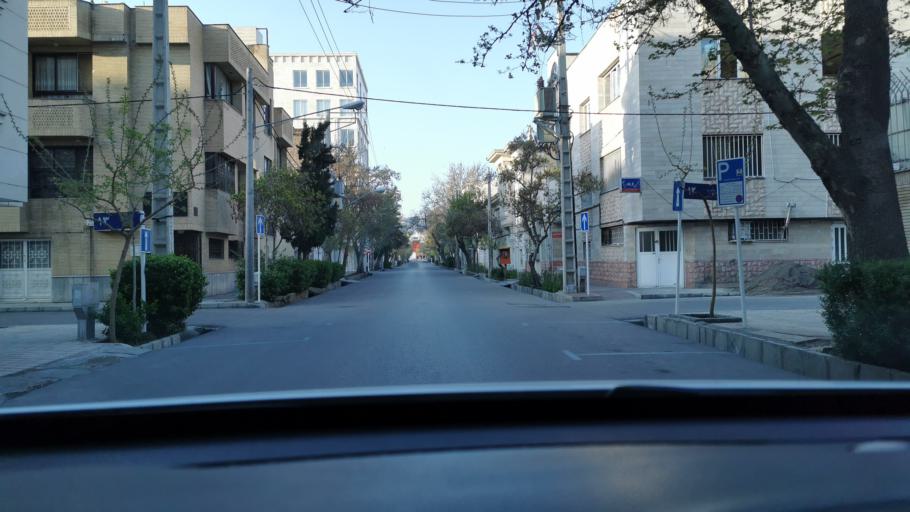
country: IR
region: Razavi Khorasan
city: Mashhad
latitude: 36.2980
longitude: 59.5800
